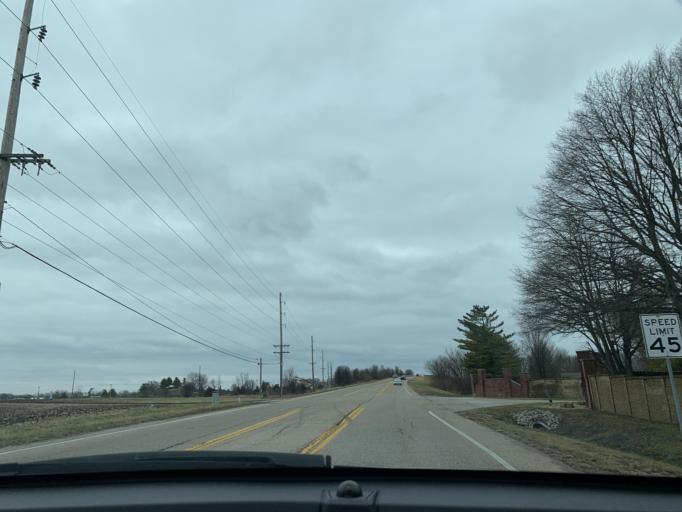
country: US
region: Illinois
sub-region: Sangamon County
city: Jerome
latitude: 39.7464
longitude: -89.6866
